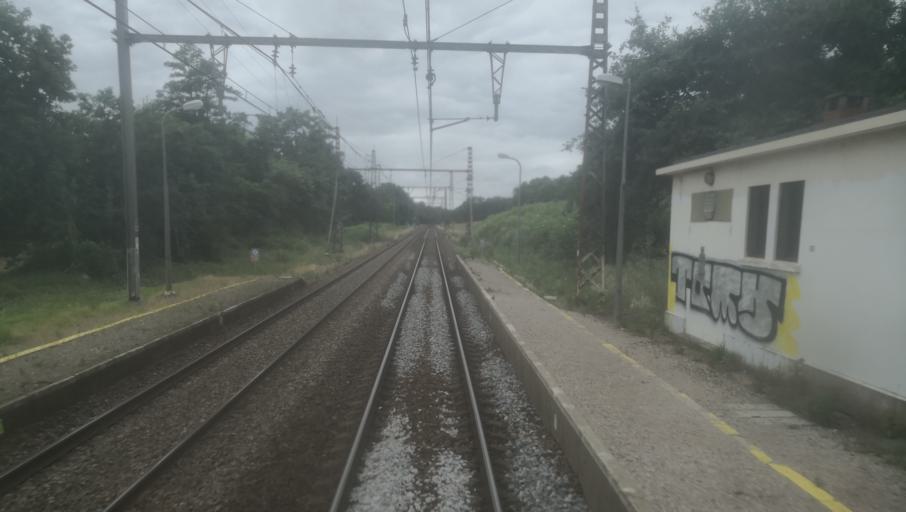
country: FR
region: Midi-Pyrenees
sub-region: Departement du Tarn-et-Garonne
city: Grisolles
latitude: 43.8658
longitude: 1.2758
